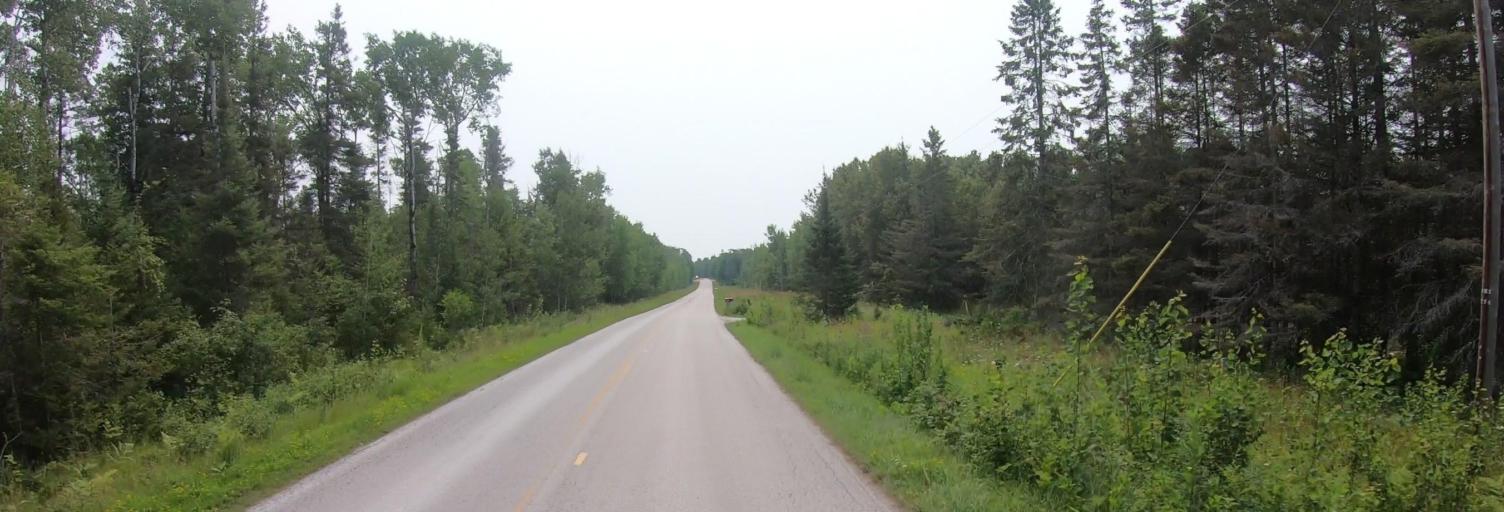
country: CA
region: Ontario
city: Thessalon
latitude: 46.0622
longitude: -83.6653
